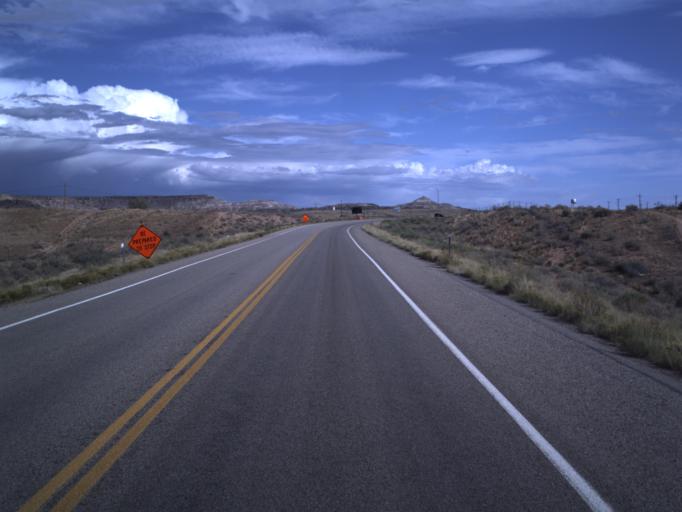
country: US
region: Colorado
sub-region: Montezuma County
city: Towaoc
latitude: 37.2090
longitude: -109.1685
